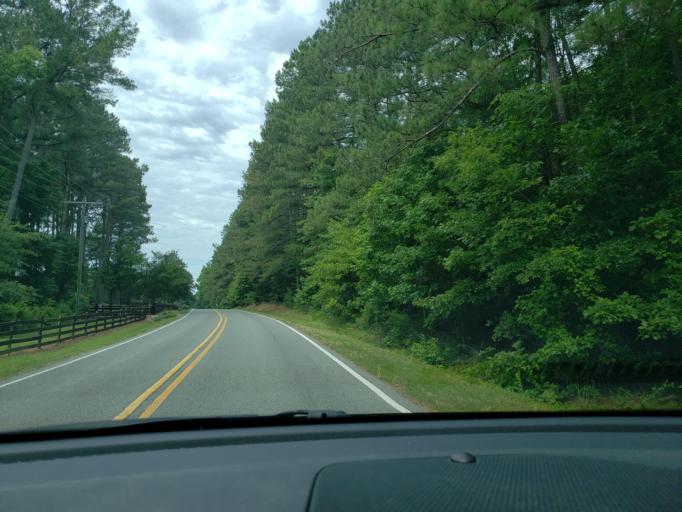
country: US
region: North Carolina
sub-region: Wake County
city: Green Level
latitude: 35.7954
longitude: -78.9818
